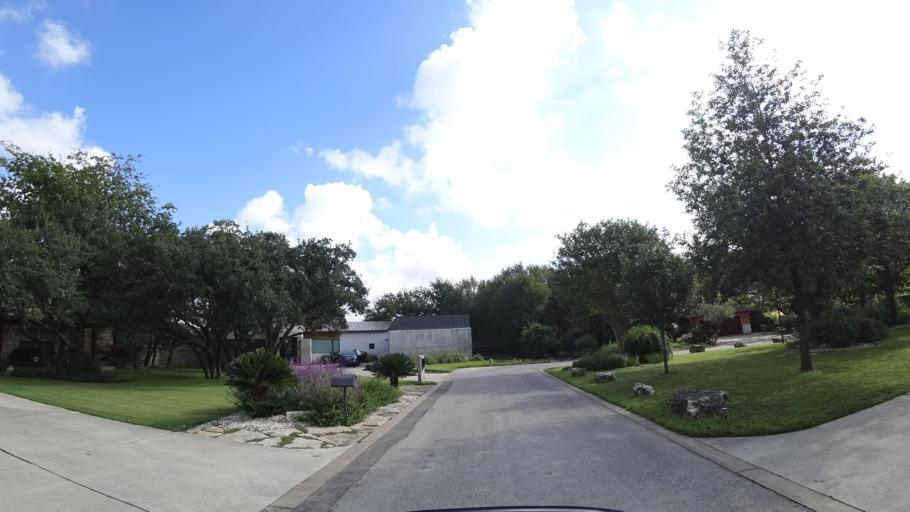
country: US
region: Texas
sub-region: Travis County
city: Rollingwood
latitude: 30.2175
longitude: -97.8132
